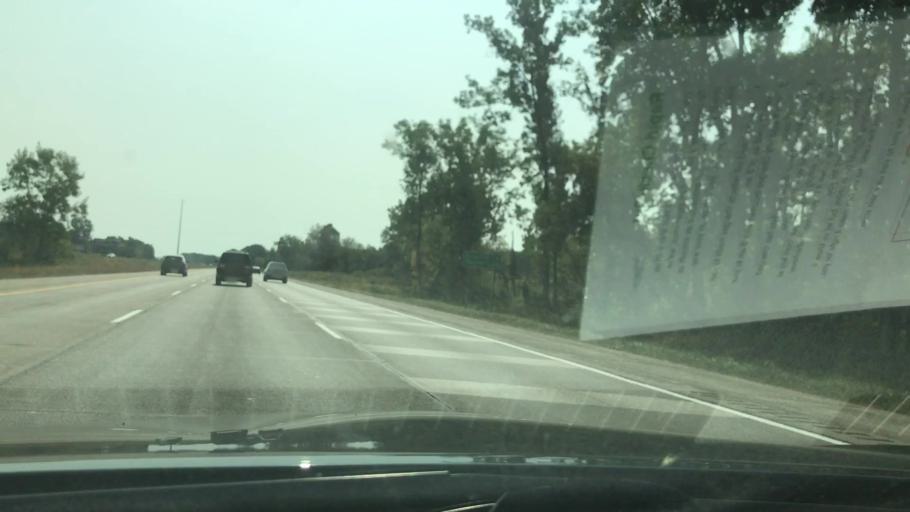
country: US
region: Michigan
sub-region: Livingston County
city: Brighton
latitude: 42.5705
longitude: -83.8455
